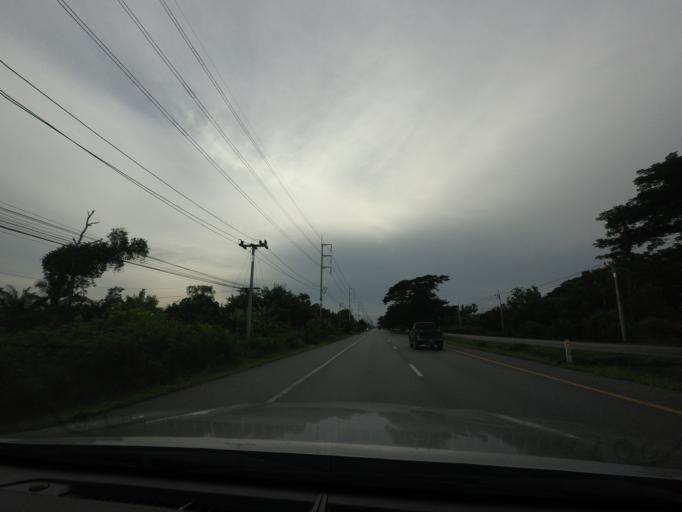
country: TH
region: Nakhon Si Thammarat
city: Chian Yai
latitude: 8.0837
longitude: 100.1588
